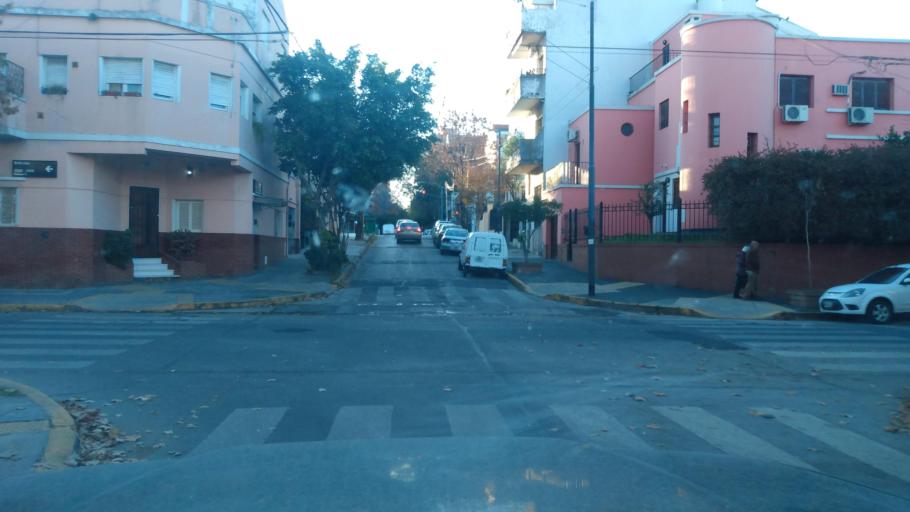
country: AR
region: Buenos Aires F.D.
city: Villa Santa Rita
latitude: -34.5820
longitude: -58.4827
